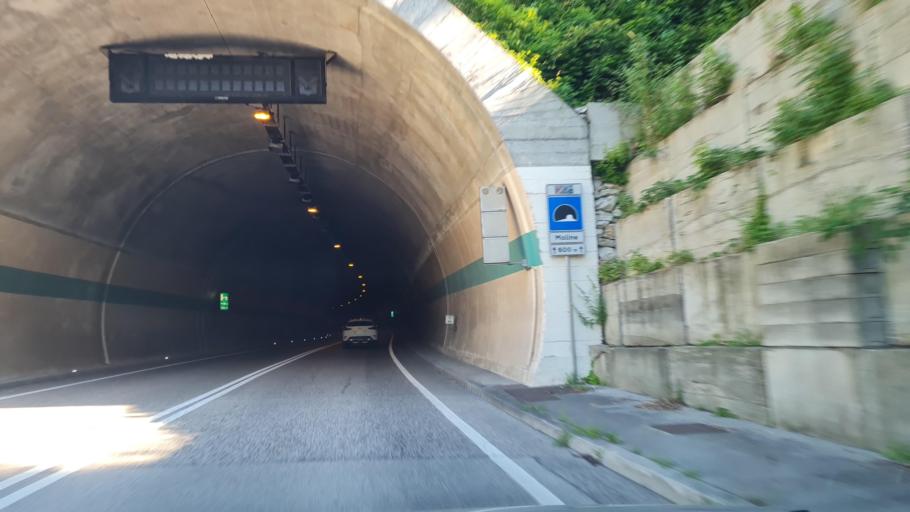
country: IT
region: Veneto
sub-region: Provincia di Belluno
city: Lamon
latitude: 46.0639
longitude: 11.7643
